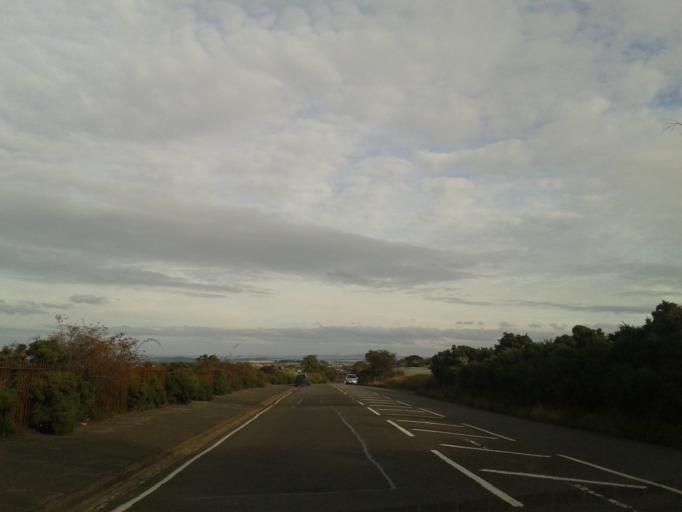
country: GB
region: Scotland
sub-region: Edinburgh
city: Edinburgh
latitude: 55.9169
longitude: -3.1906
